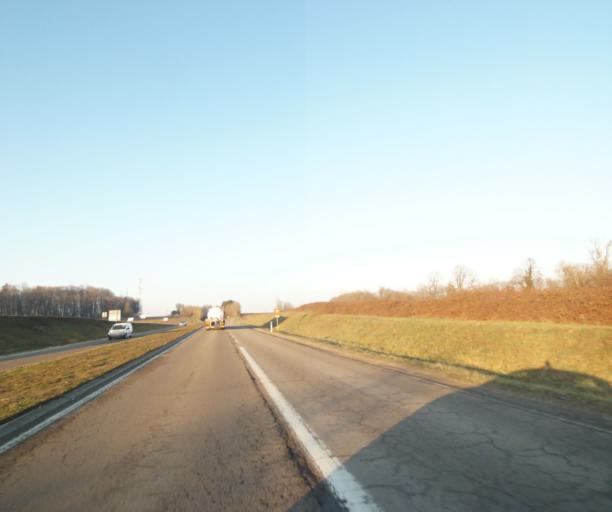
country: FR
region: Champagne-Ardenne
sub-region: Departement de la Haute-Marne
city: Bienville
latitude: 48.5721
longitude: 5.0353
